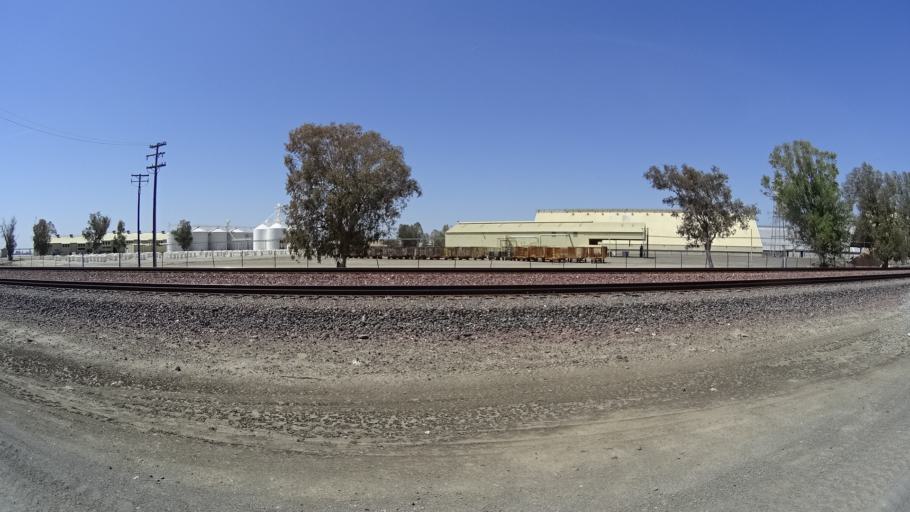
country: US
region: California
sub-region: Kings County
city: Corcoran
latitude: 36.0896
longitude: -119.5501
